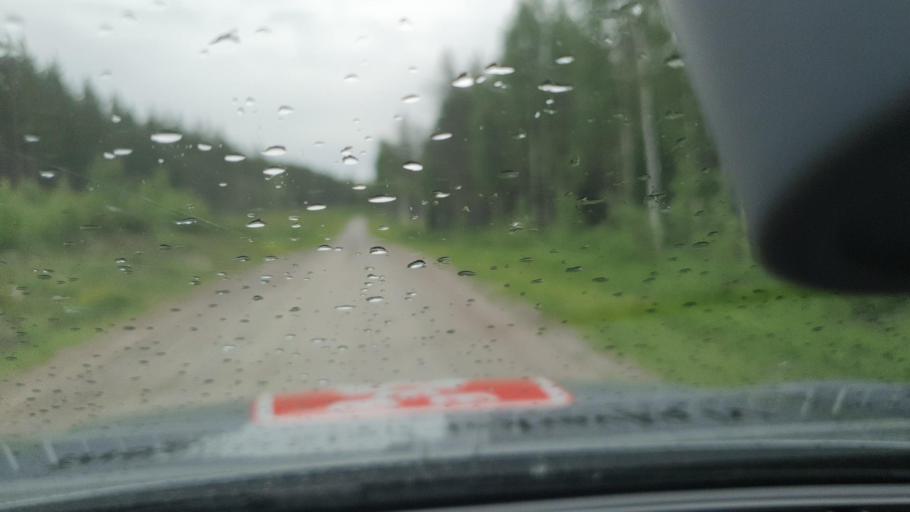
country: SE
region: Norrbotten
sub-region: Kalix Kommun
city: Rolfs
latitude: 66.0182
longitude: 23.1076
